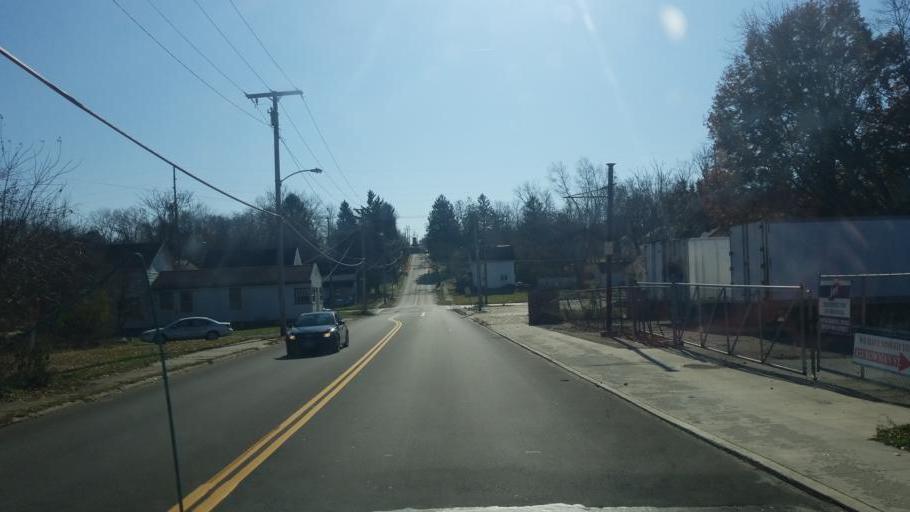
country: US
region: Ohio
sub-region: Richland County
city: Mansfield
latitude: 40.7663
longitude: -82.5232
